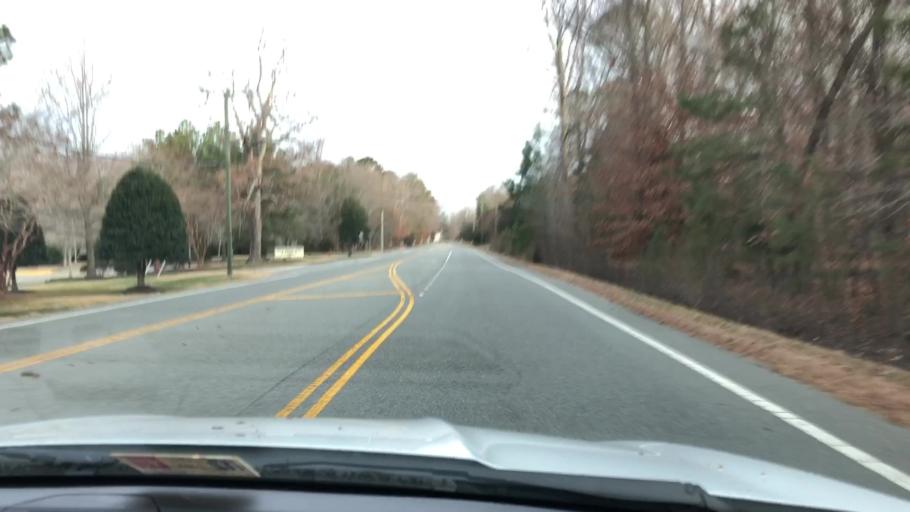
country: US
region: Virginia
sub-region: James City County
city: Williamsburg
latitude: 37.2664
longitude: -76.7409
